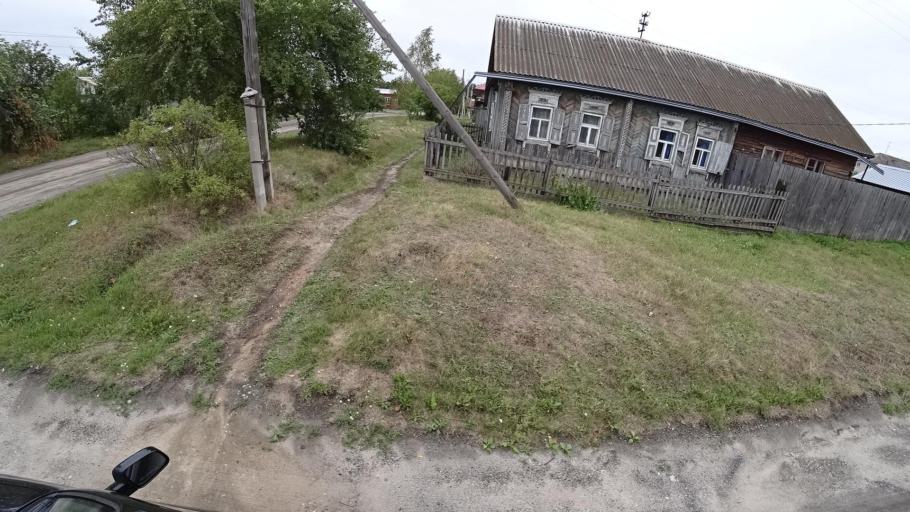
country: RU
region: Sverdlovsk
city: Kamyshlov
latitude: 56.8381
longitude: 62.7203
